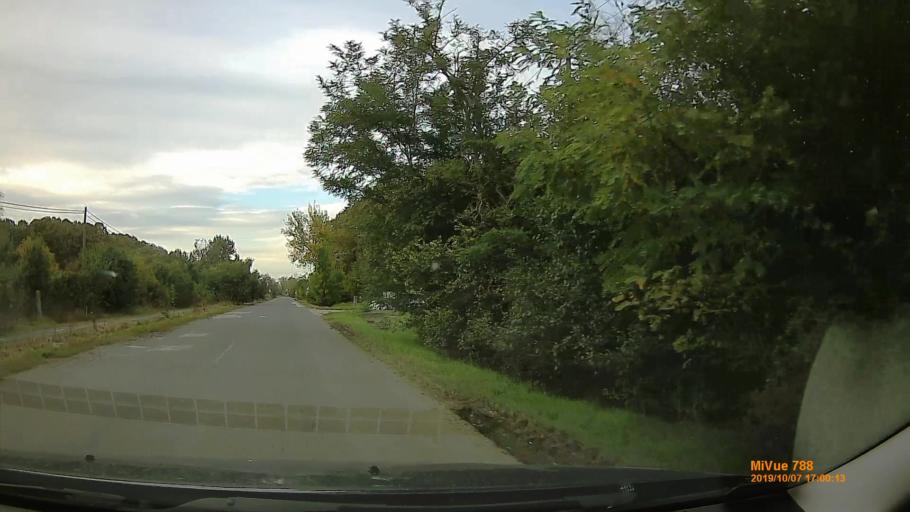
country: HU
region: Bekes
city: Szarvas
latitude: 46.8456
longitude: 20.5722
